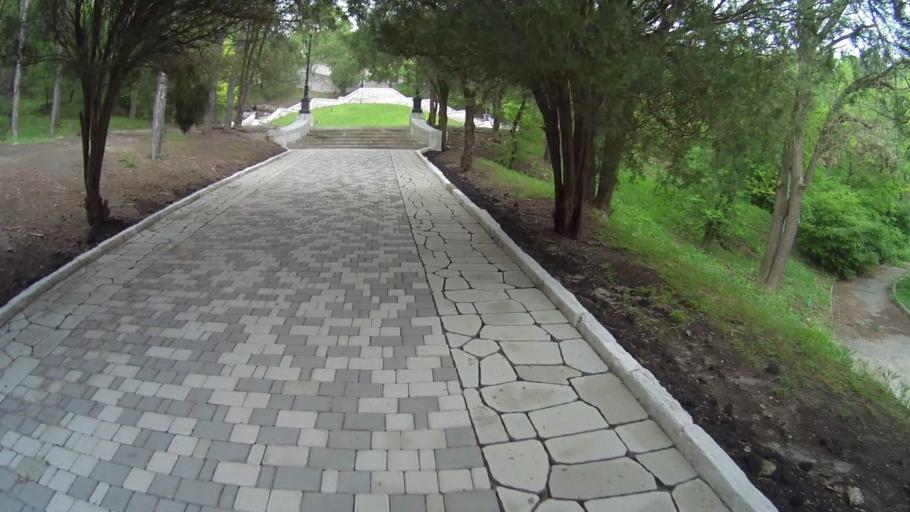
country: RU
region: Stavropol'skiy
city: Goryachevodskiy
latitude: 44.0393
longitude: 43.0872
